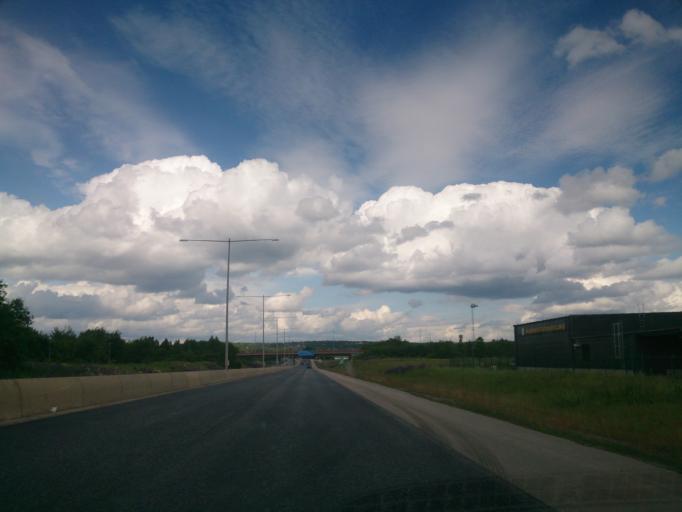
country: SE
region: OEstergoetland
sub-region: Norrkopings Kommun
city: Jursla
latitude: 58.6474
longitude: 16.1647
